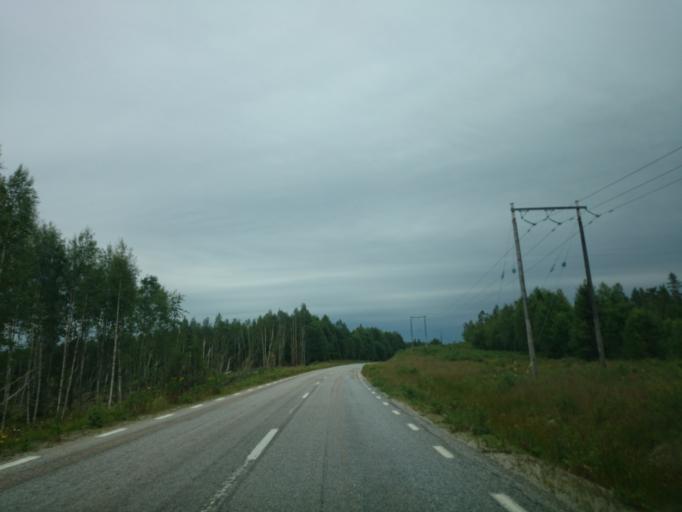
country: SE
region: Vaesternorrland
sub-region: Sundsvalls Kommun
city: Njurundabommen
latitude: 62.2236
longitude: 17.4488
